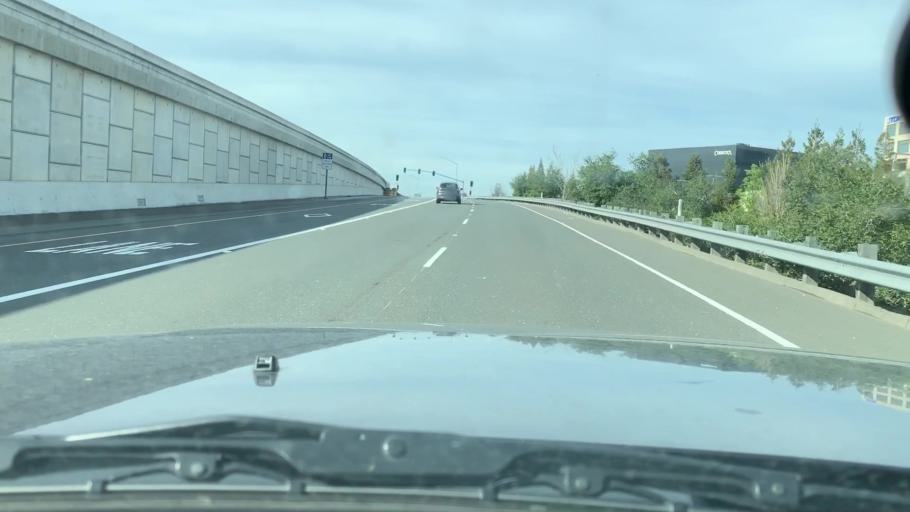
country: US
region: California
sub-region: Santa Clara County
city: San Jose
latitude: 37.3662
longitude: -121.9203
